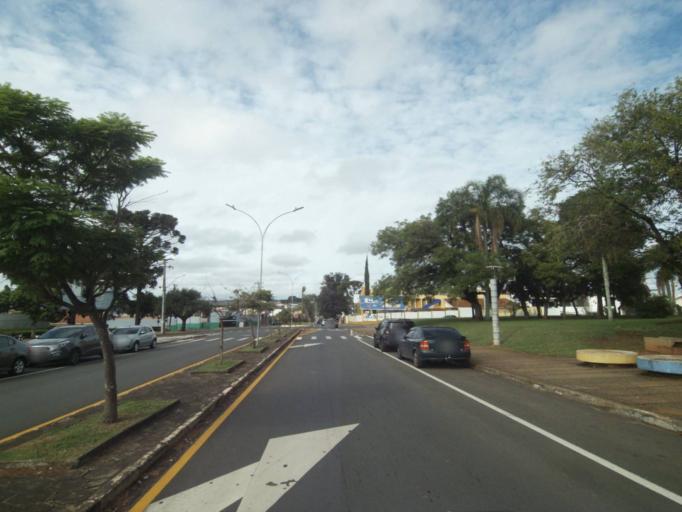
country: BR
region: Parana
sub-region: Telemaco Borba
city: Telemaco Borba
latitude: -24.3308
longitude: -50.6220
